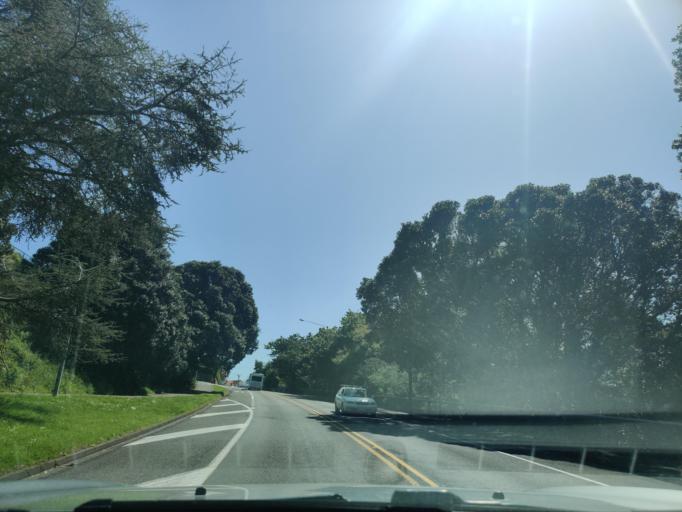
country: NZ
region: Manawatu-Wanganui
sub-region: Wanganui District
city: Wanganui
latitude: -39.9211
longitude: 175.0388
